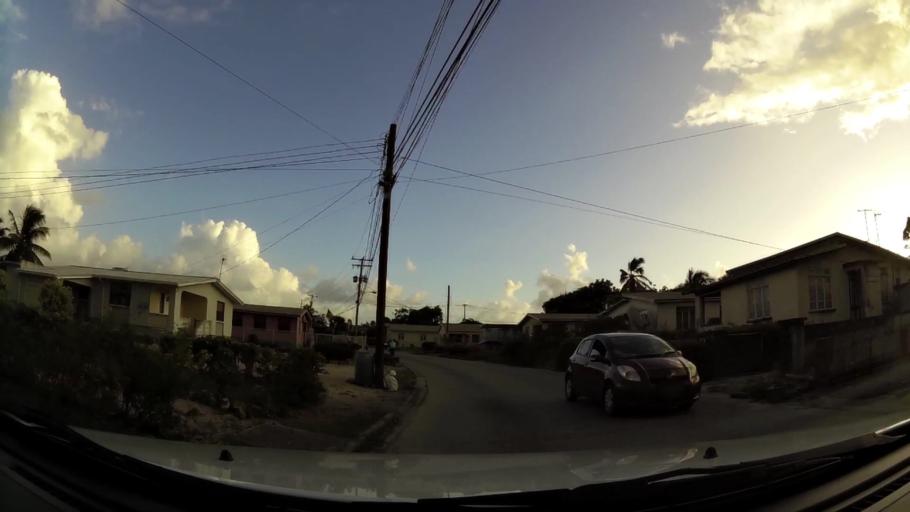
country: BB
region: Saint Philip
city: Crane
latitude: 13.1059
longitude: -59.4683
